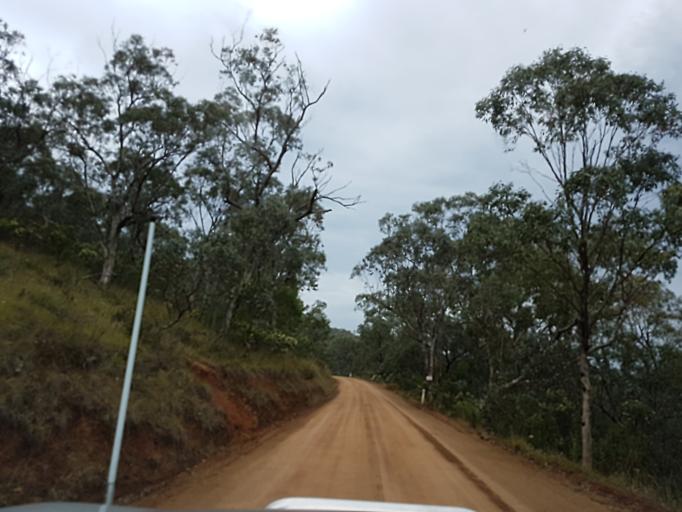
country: AU
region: New South Wales
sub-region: Snowy River
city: Jindabyne
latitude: -36.9311
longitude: 148.3559
